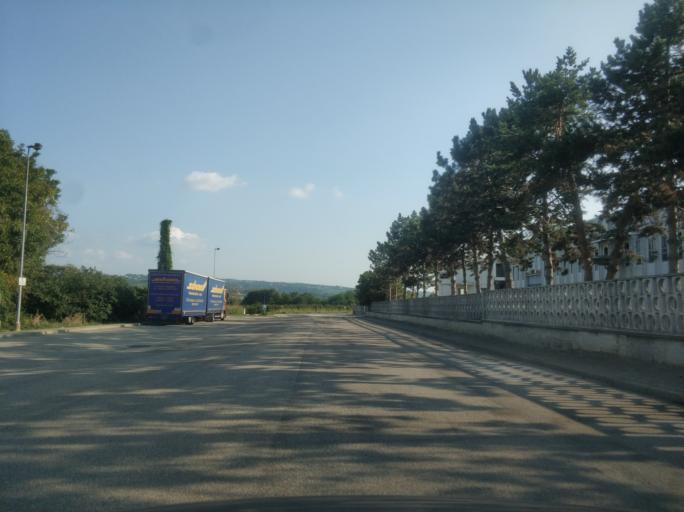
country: IT
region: Piedmont
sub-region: Provincia di Cuneo
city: Cinzano
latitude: 44.6902
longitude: 7.9009
